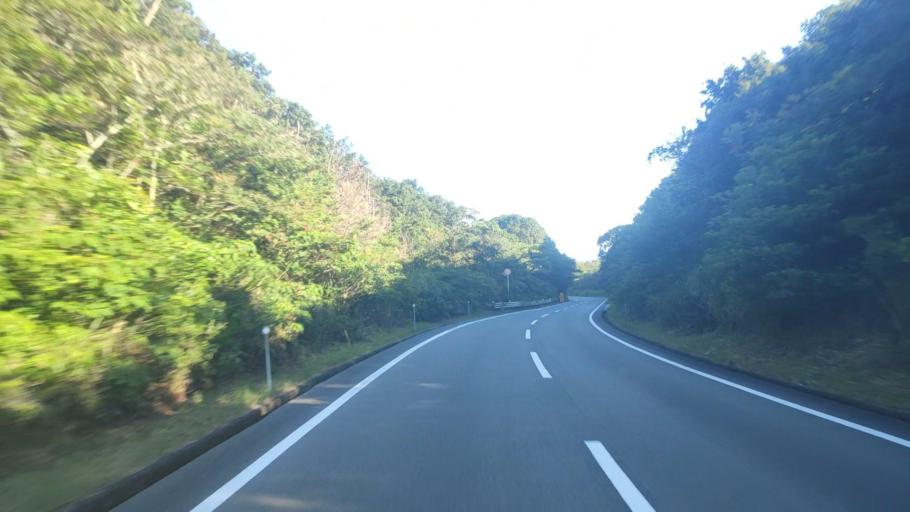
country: JP
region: Mie
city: Toba
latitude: 34.4207
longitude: 136.9138
